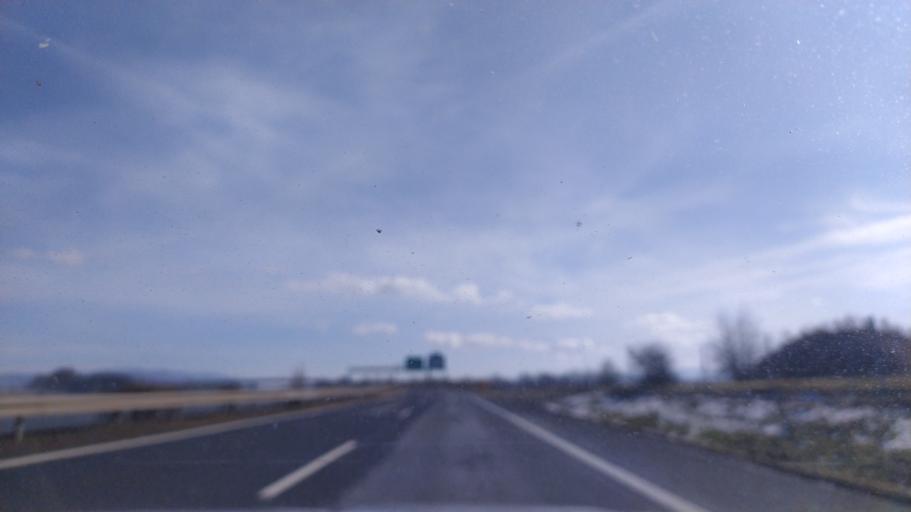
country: CZ
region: Karlovarsky
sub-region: Okres Cheb
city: Cheb
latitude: 50.0907
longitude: 12.4158
